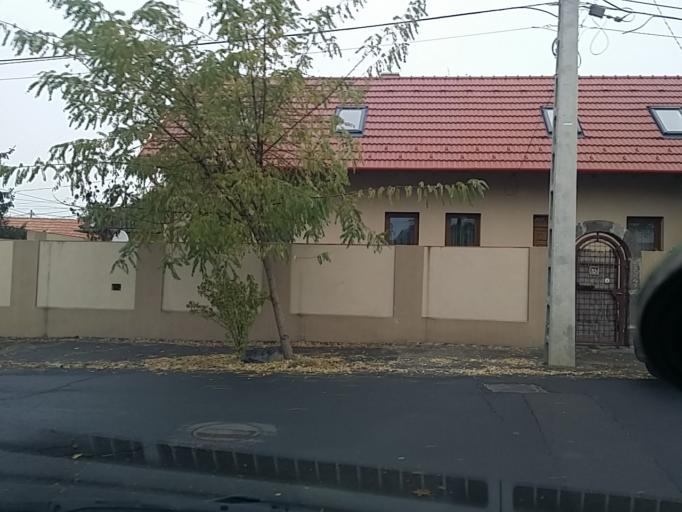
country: HU
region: Heves
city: Gyongyos
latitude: 47.7876
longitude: 19.9282
